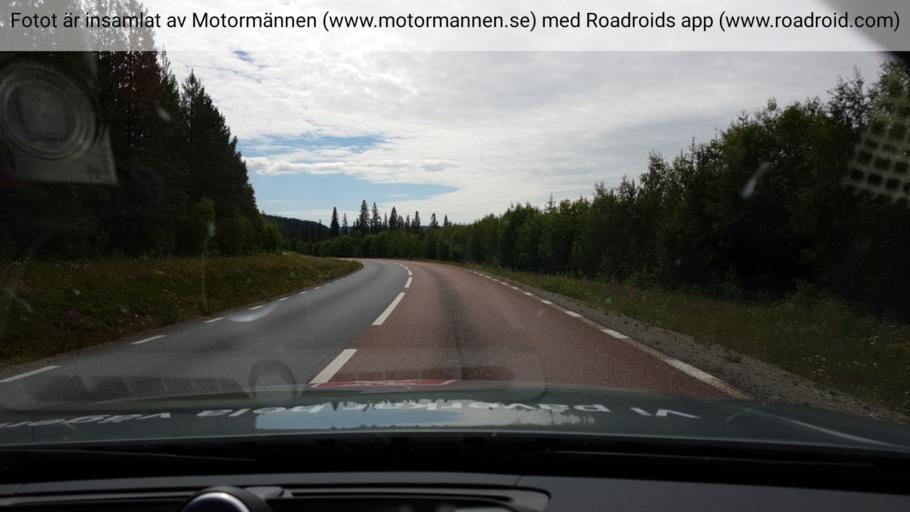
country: SE
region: Vaesterbotten
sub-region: Dorotea Kommun
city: Dorotea
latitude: 64.1413
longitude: 16.2232
